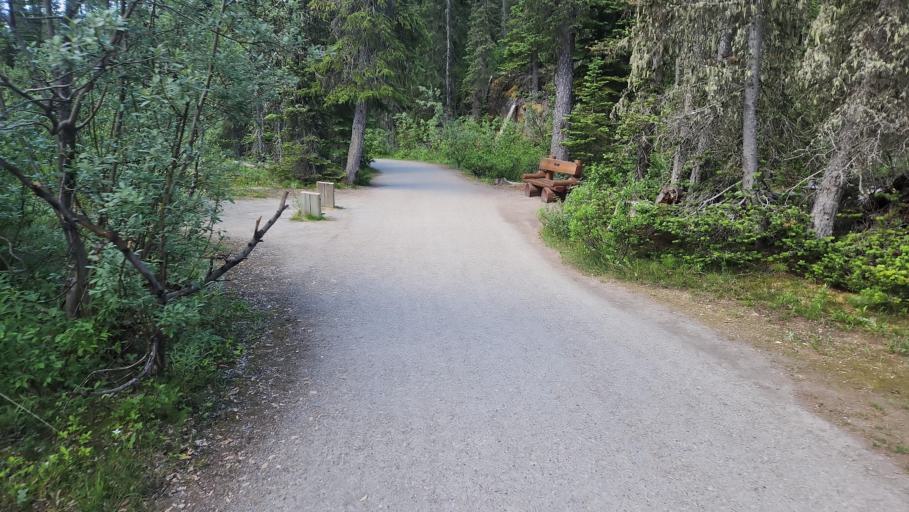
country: CA
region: Alberta
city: Lake Louise
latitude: 51.4966
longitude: -116.4824
